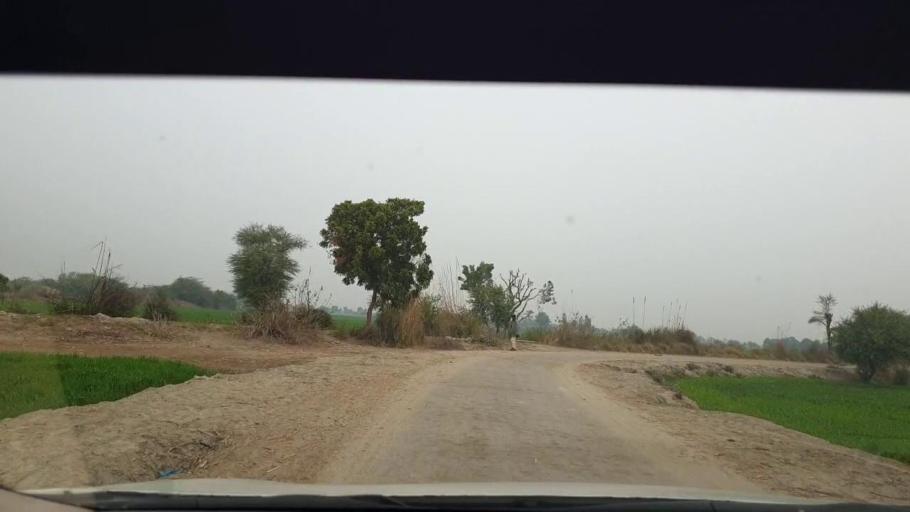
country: PK
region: Sindh
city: Berani
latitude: 25.8721
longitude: 68.8261
